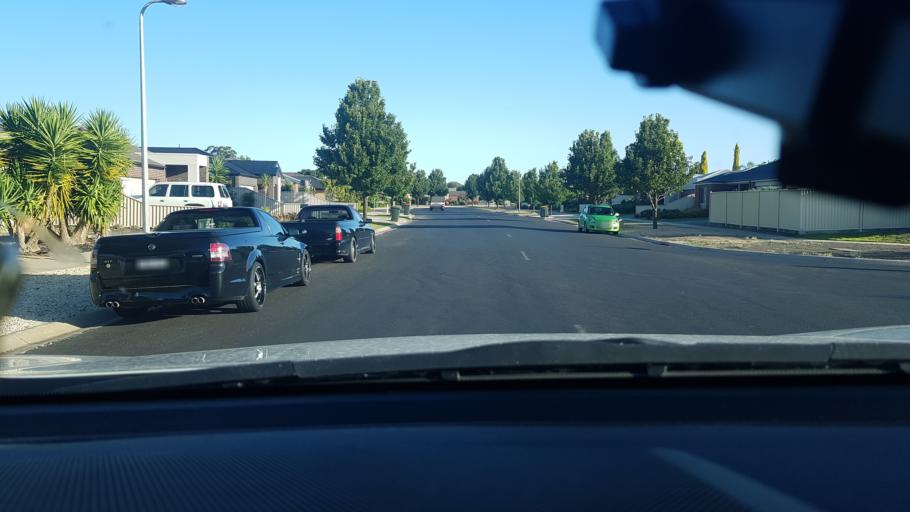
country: AU
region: Victoria
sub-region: Horsham
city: Horsham
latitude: -36.7132
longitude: 142.1793
